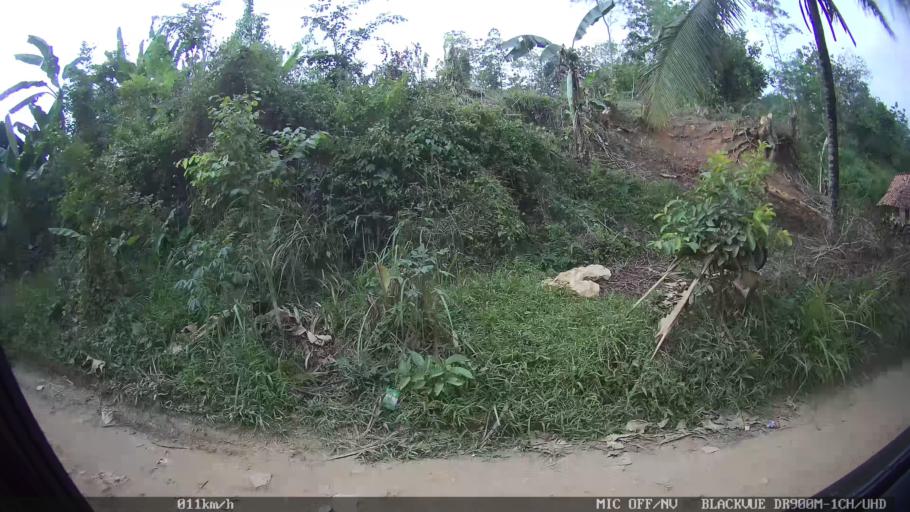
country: ID
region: Lampung
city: Gadingrejo
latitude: -5.3920
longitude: 105.0221
